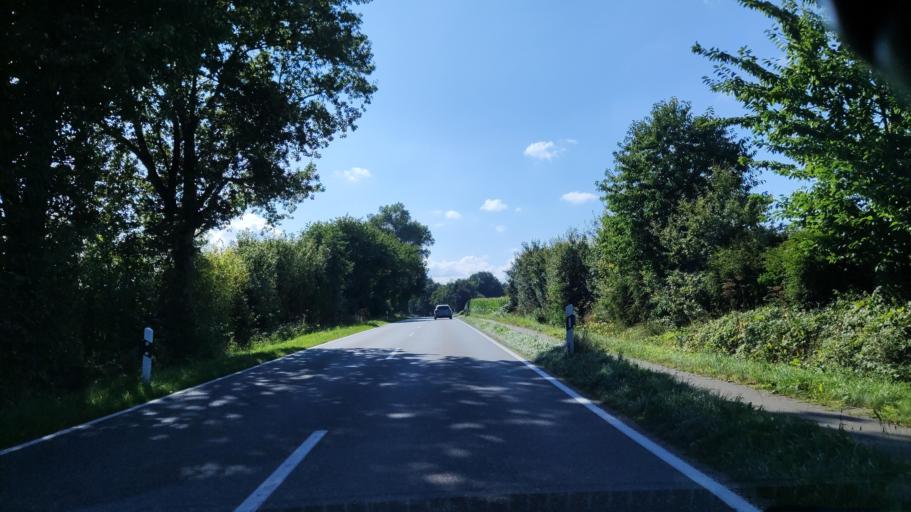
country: DE
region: Schleswig-Holstein
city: Osterby
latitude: 54.4475
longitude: 9.7473
